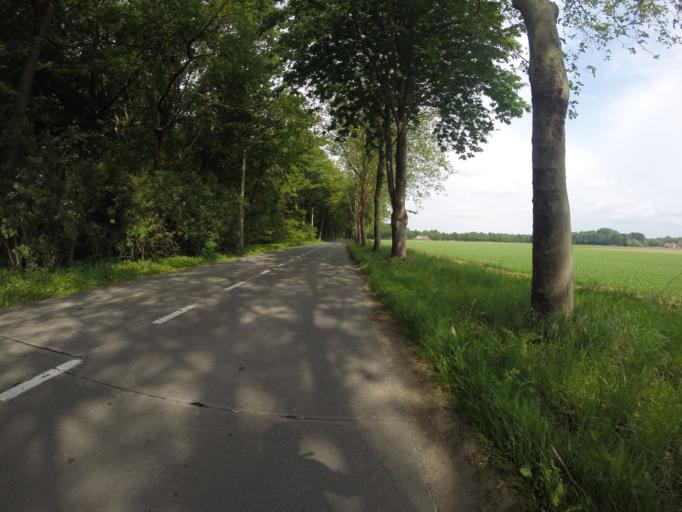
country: BE
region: Flanders
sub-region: Provincie West-Vlaanderen
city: Ruiselede
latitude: 51.0719
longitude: 3.3647
